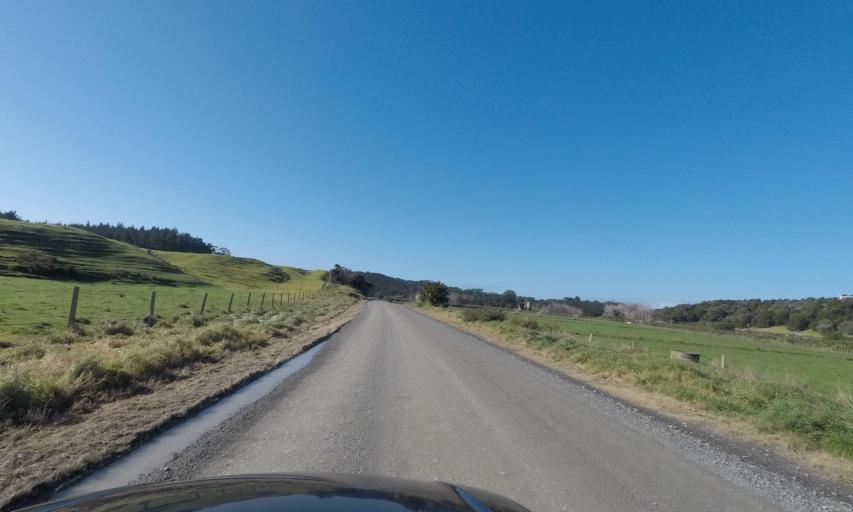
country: NZ
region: Auckland
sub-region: Auckland
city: Wellsford
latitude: -36.1597
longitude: 174.6278
